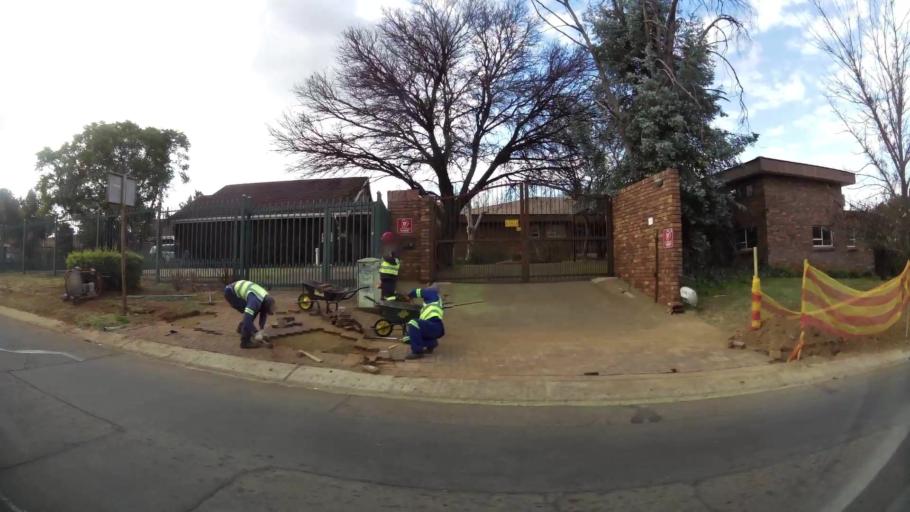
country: ZA
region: Orange Free State
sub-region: Mangaung Metropolitan Municipality
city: Bloemfontein
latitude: -29.0816
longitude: 26.2019
